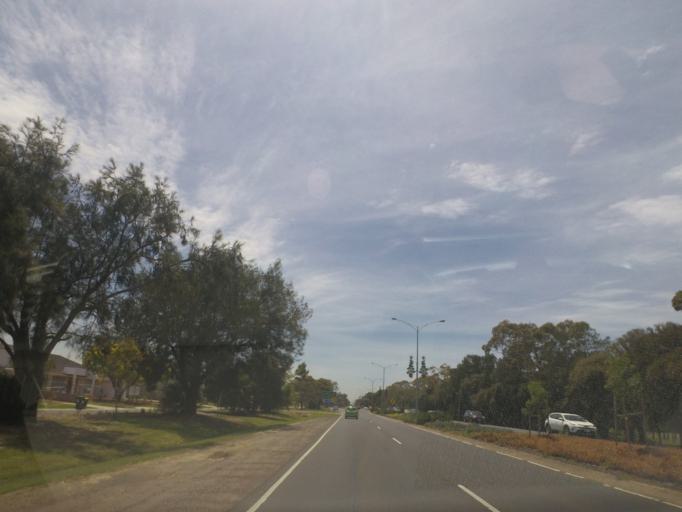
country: AU
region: Victoria
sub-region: Wyndham
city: Werribee
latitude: -37.8949
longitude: 144.6781
